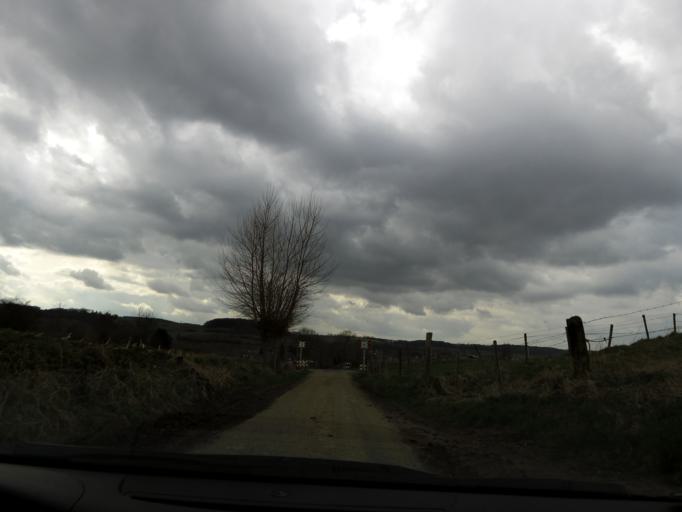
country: NL
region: Limburg
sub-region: Valkenburg aan de Geul
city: Schin op Geul
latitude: 50.8541
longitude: 5.8803
